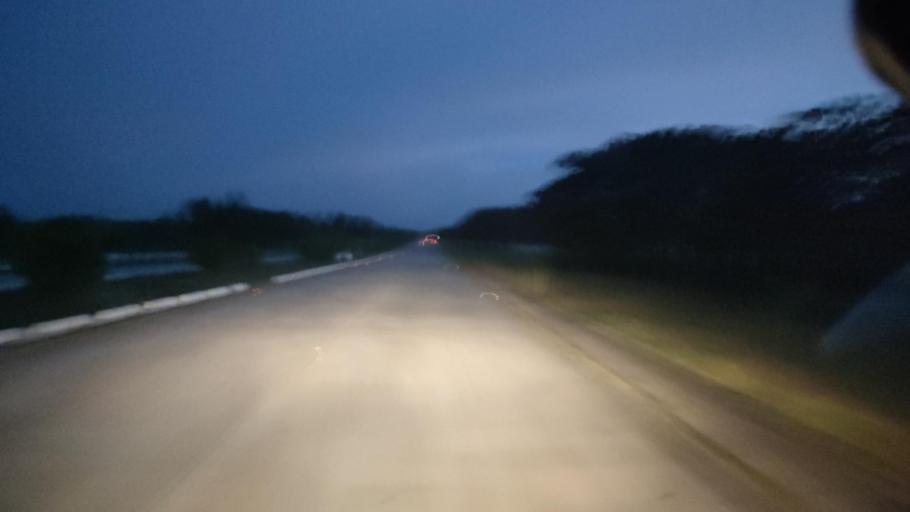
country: MM
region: Mandalay
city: Nay Pyi Taw
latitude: 19.9705
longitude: 95.9891
